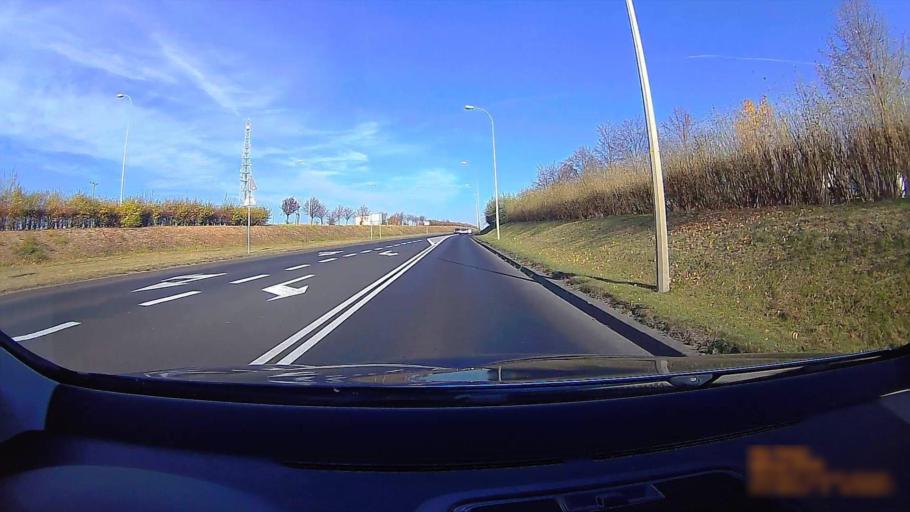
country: PL
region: Greater Poland Voivodeship
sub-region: Kalisz
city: Kalisz
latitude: 51.7788
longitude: 18.0801
